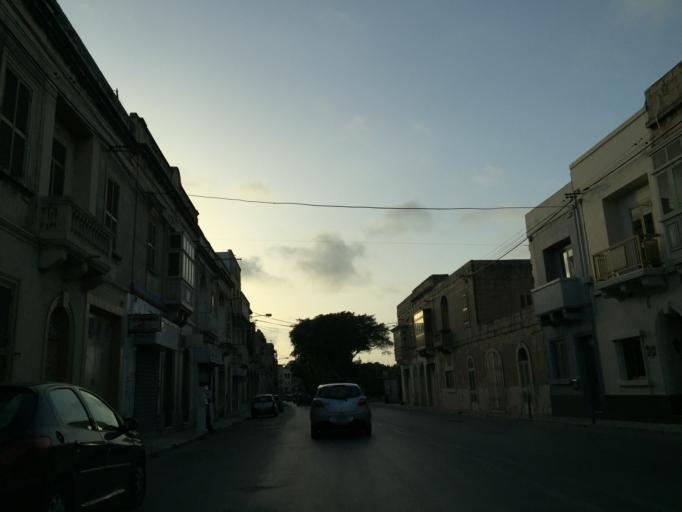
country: MT
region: Saint Paul's Bay
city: San Pawl il-Bahar
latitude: 35.9360
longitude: 14.4138
